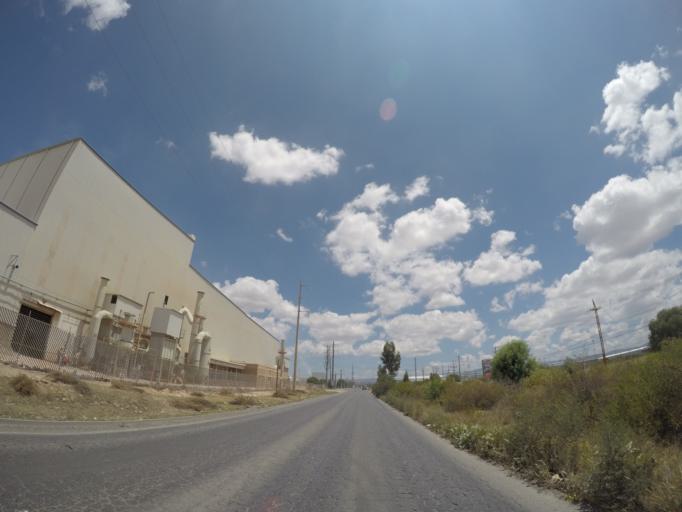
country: MX
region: San Luis Potosi
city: La Pila
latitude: 22.0484
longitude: -100.8716
